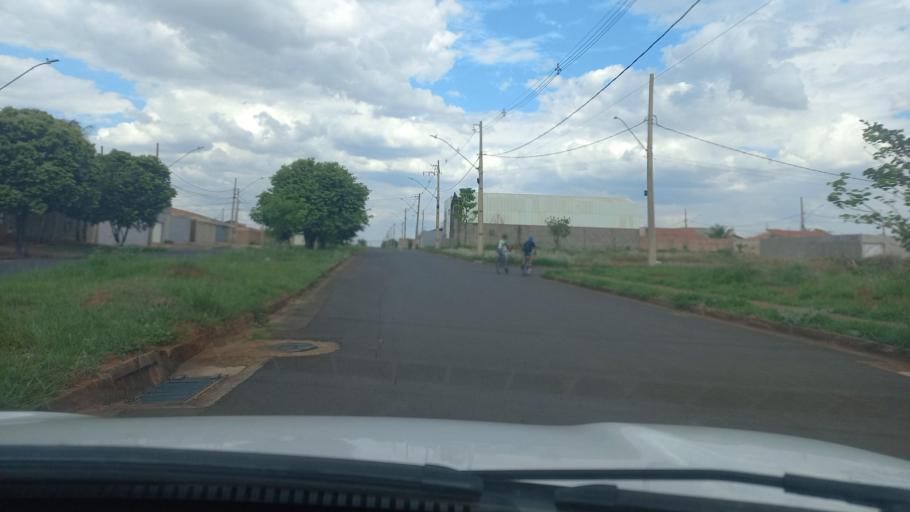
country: BR
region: Minas Gerais
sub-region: Uberaba
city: Uberaba
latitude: -19.7577
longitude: -47.9958
